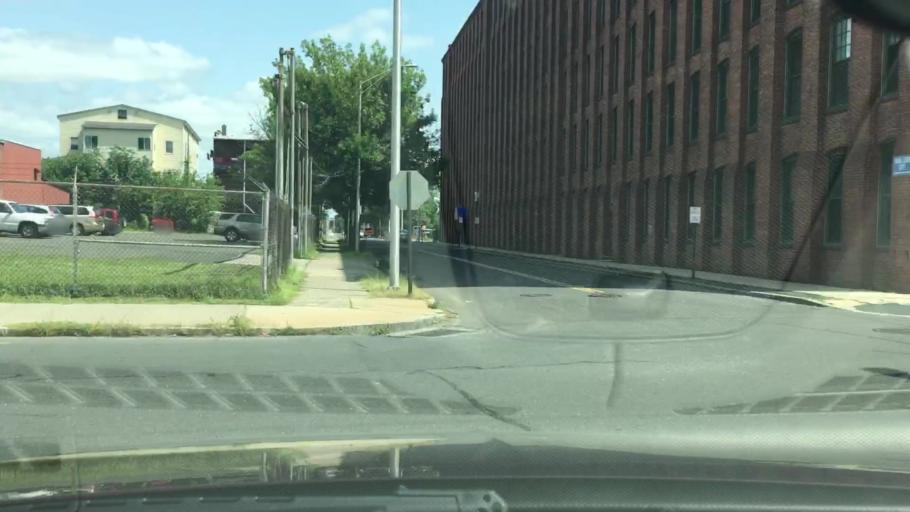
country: US
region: Connecticut
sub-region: Hartford County
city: New Britain
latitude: 41.6710
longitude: -72.7872
